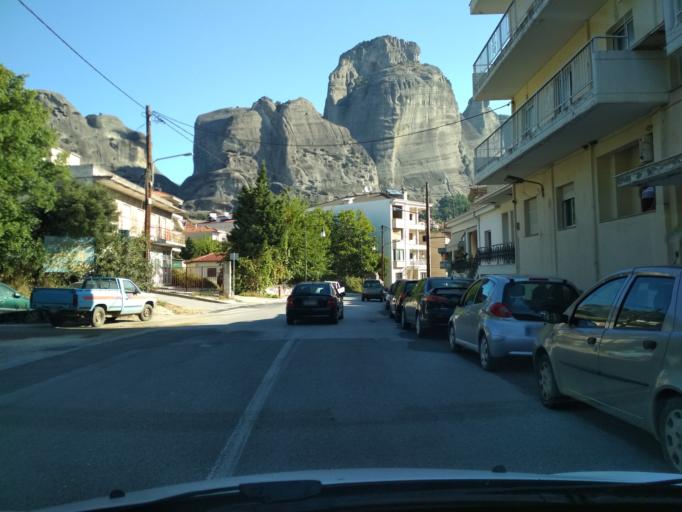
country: GR
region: Thessaly
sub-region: Trikala
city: Kalampaka
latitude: 39.7045
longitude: 21.6181
